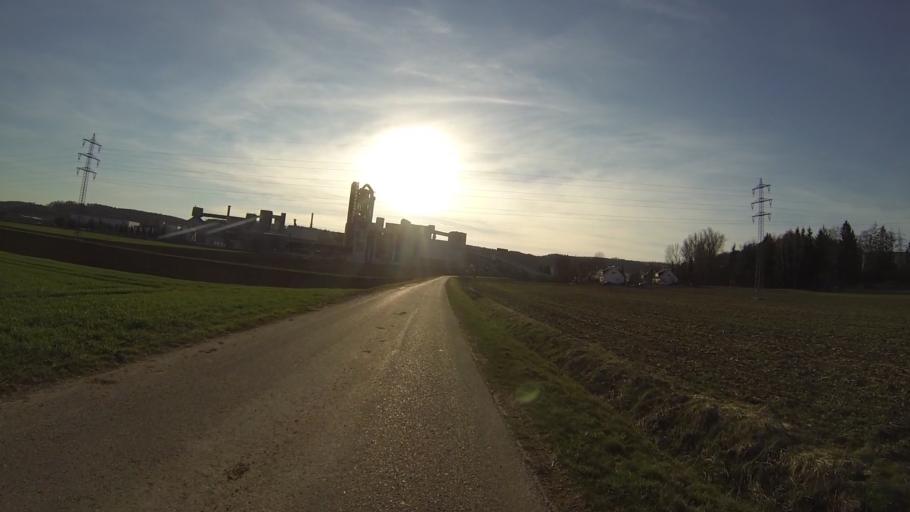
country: DE
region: Baden-Wuerttemberg
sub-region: Regierungsbezirk Stuttgart
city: Heidenheim an der Brenz
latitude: 48.6541
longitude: 10.1693
